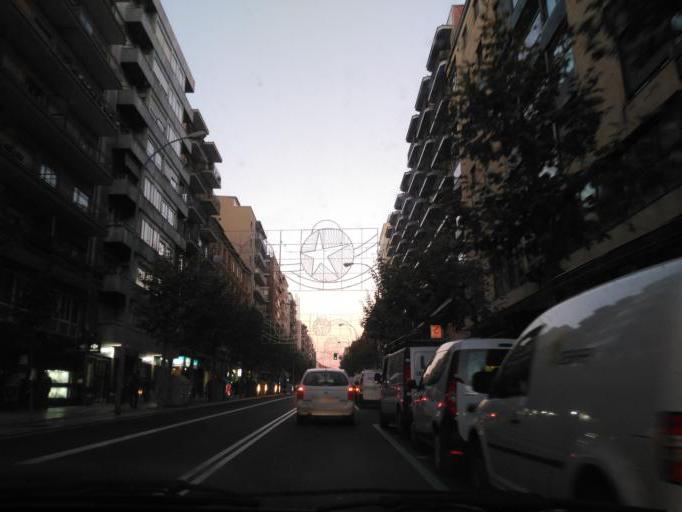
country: ES
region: Castille and Leon
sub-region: Provincia de Salamanca
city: Salamanca
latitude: 40.9696
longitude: -5.6591
